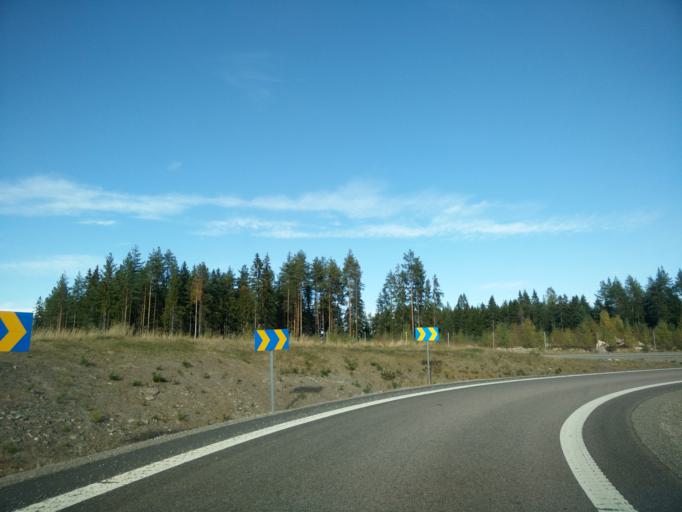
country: SE
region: Gaevleborg
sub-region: Hudiksvalls Kommun
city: Iggesund
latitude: 61.5529
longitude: 16.9757
